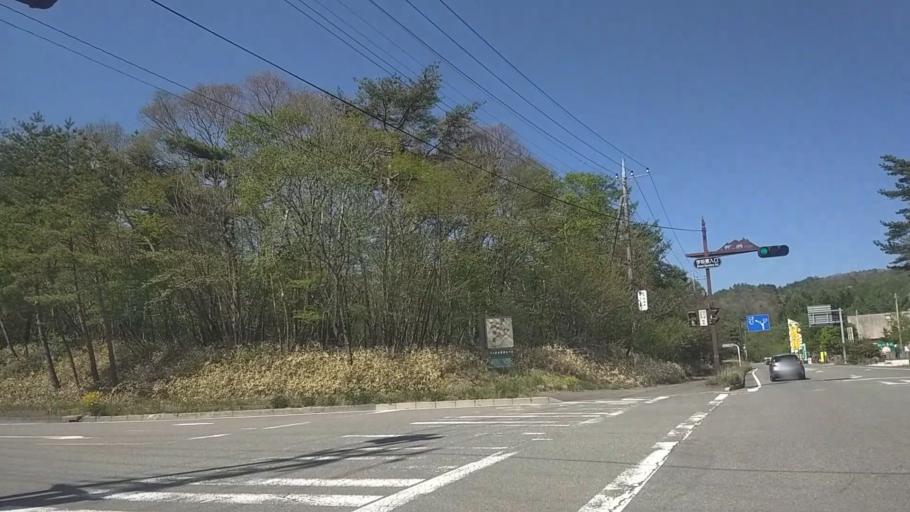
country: JP
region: Yamanashi
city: Nirasaki
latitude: 35.9308
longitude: 138.4451
